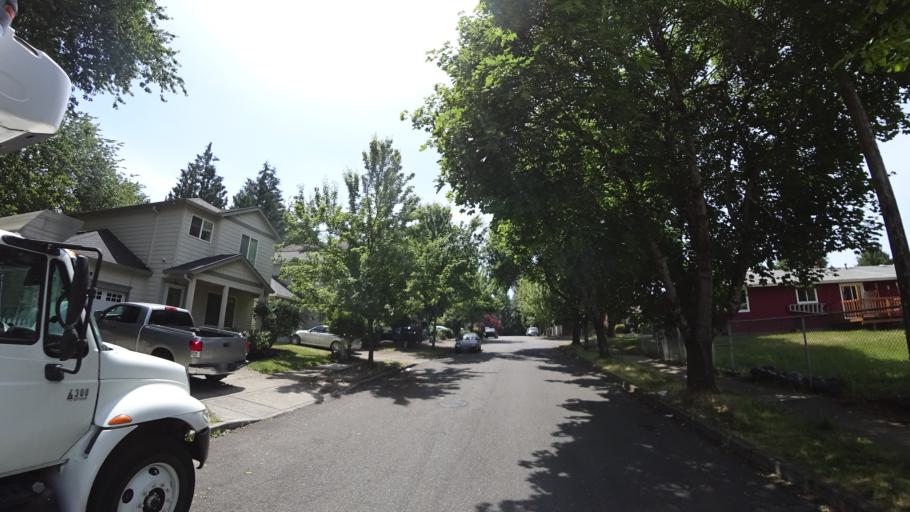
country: US
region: Oregon
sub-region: Multnomah County
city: Fairview
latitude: 45.5495
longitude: -122.5040
